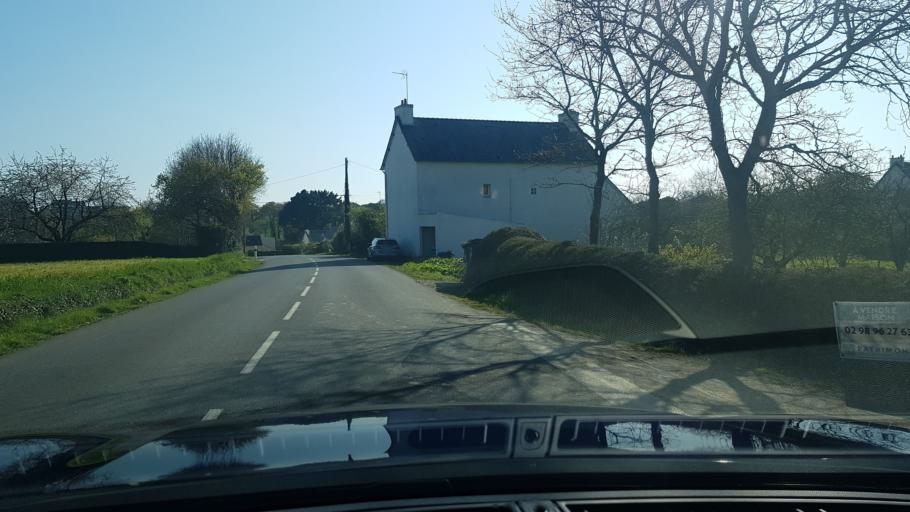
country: FR
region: Brittany
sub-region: Departement du Finistere
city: Clohars-Carnoet
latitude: 47.7790
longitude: -3.5933
